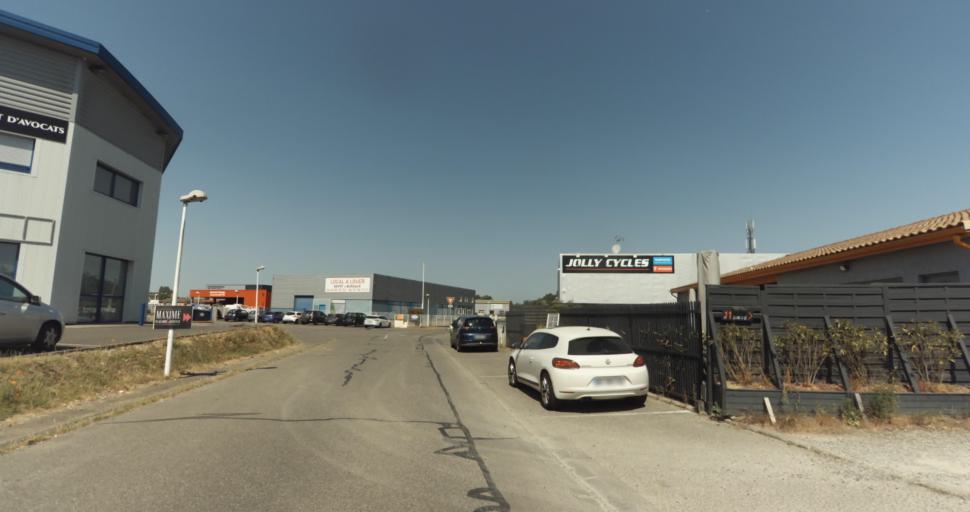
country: FR
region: Midi-Pyrenees
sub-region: Departement de la Haute-Garonne
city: La Salvetat-Saint-Gilles
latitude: 43.5834
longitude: 1.2769
